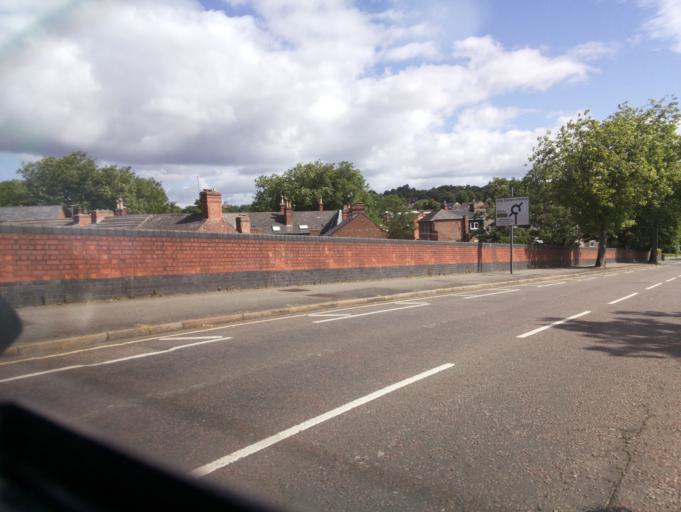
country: GB
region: England
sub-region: Nottingham
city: Nottingham
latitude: 52.9461
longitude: -1.1730
